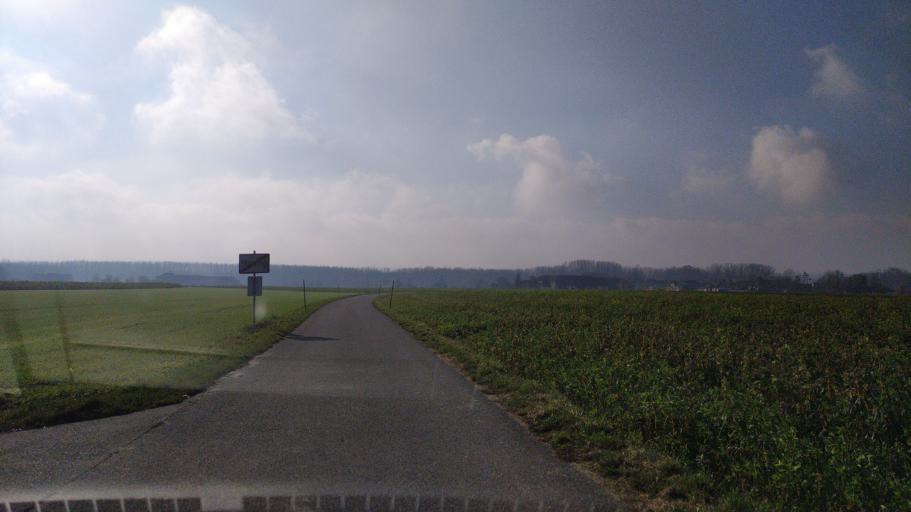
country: AT
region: Lower Austria
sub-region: Politischer Bezirk Amstetten
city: Strengberg
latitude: 48.1879
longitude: 14.6529
